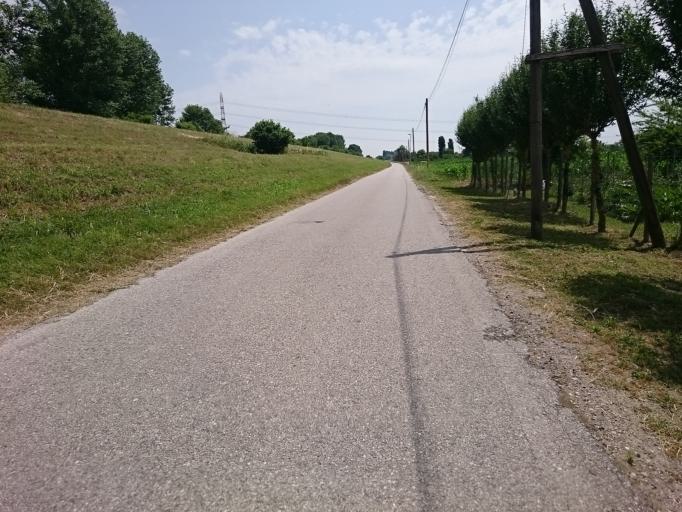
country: IT
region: Veneto
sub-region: Provincia di Padova
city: Codevigo
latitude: 45.2309
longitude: 12.1257
